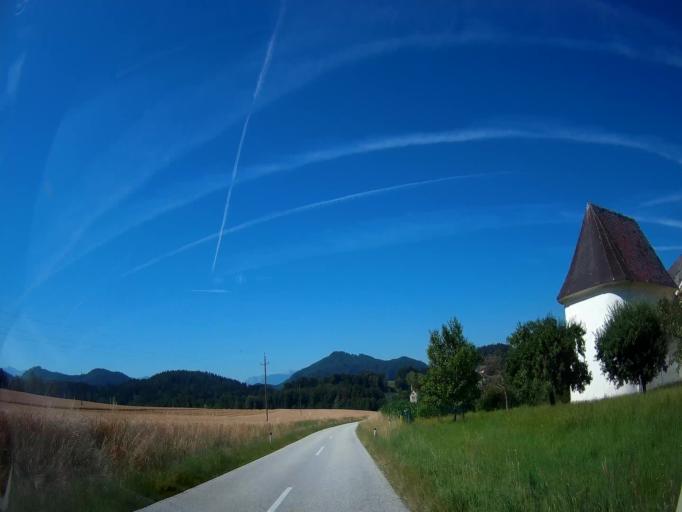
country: AT
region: Carinthia
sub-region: Politischer Bezirk Klagenfurt Land
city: Maria Saal
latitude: 46.6939
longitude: 14.3666
